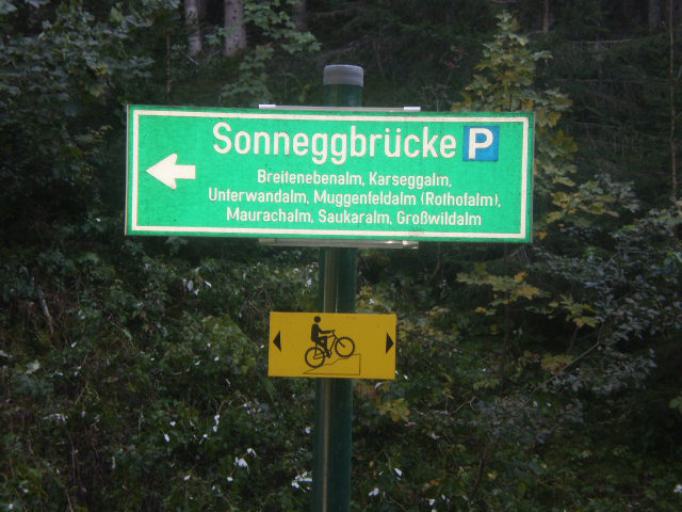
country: AT
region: Salzburg
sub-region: Politischer Bezirk Sankt Johann im Pongau
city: Sankt Johann im Pongau
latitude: 47.2752
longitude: 13.2207
